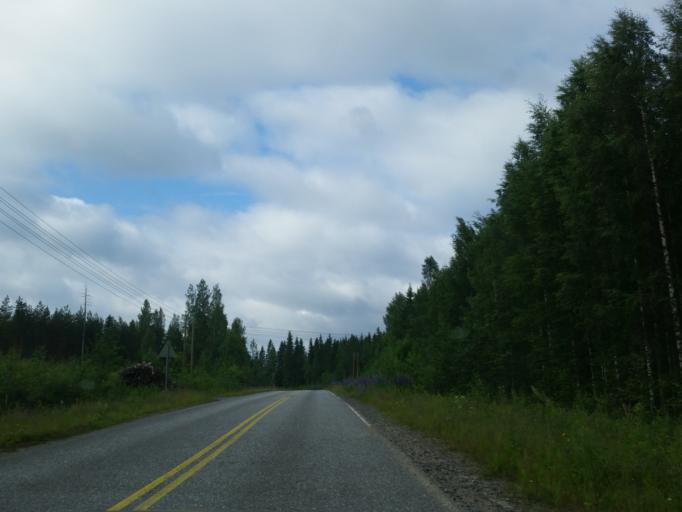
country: FI
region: Northern Savo
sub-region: Sisae-Savo
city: Tervo
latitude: 63.0272
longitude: 26.6896
